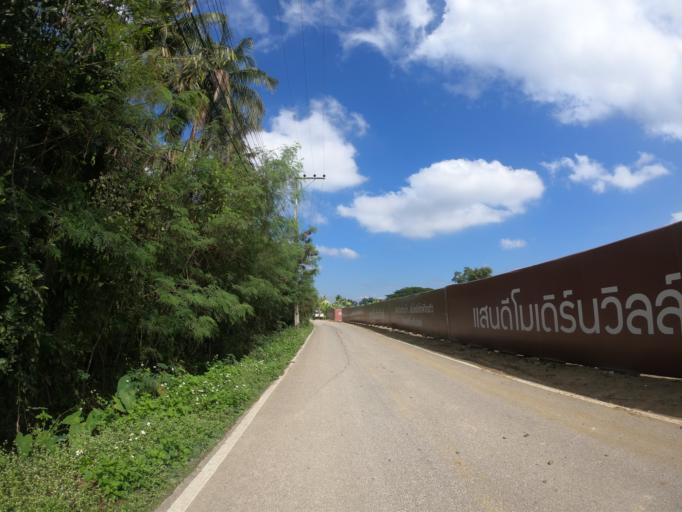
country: TH
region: Chiang Mai
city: Saraphi
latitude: 18.7194
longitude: 99.0184
